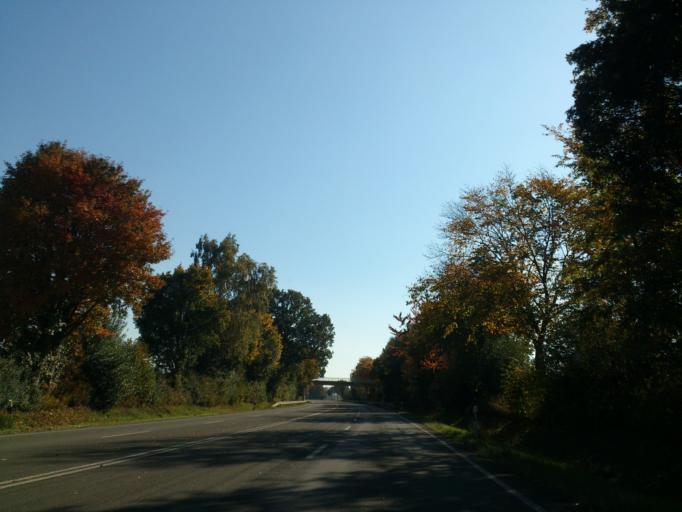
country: DE
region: Hesse
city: Liebenau
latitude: 51.4368
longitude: 9.3037
